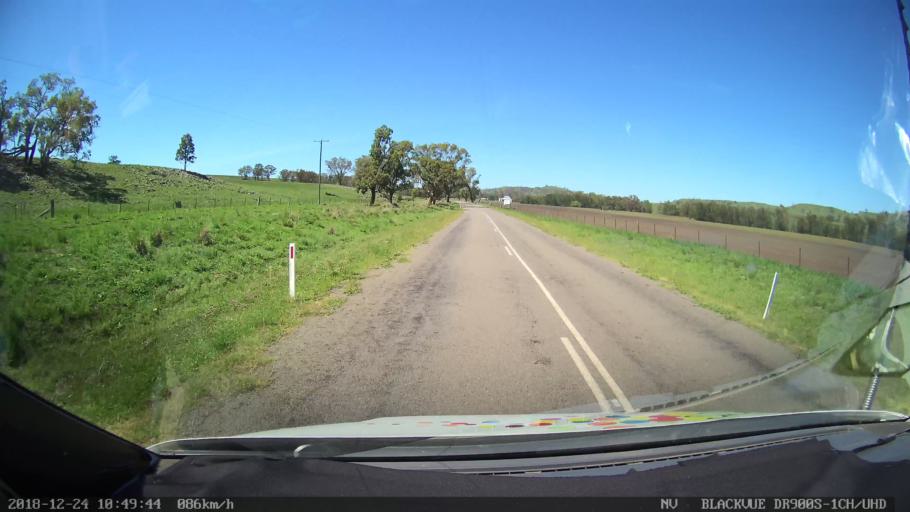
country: AU
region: New South Wales
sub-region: Upper Hunter Shire
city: Merriwa
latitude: -31.9511
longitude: 150.4261
